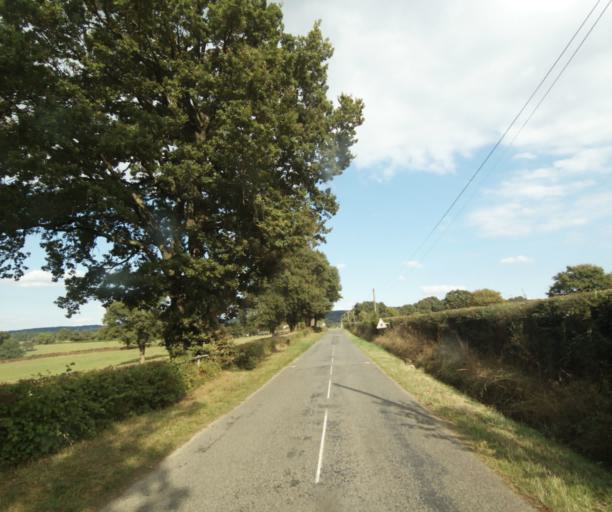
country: FR
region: Bourgogne
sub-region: Departement de Saone-et-Loire
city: Palinges
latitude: 46.5066
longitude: 4.2518
